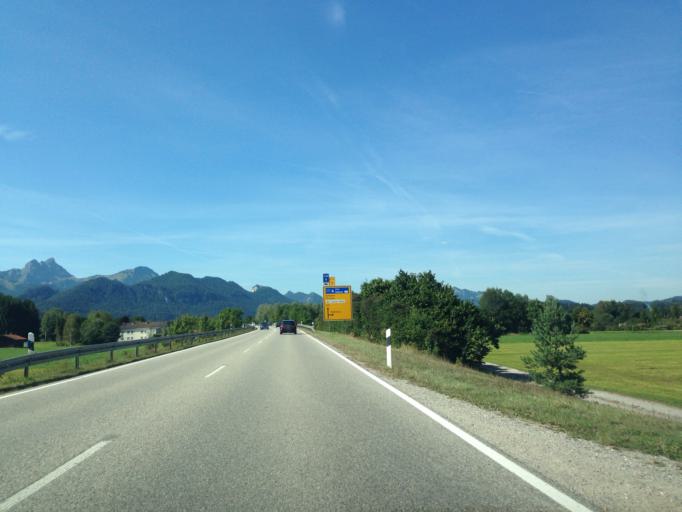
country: DE
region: Bavaria
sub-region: Swabia
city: Fuessen
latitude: 47.5803
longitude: 10.6838
